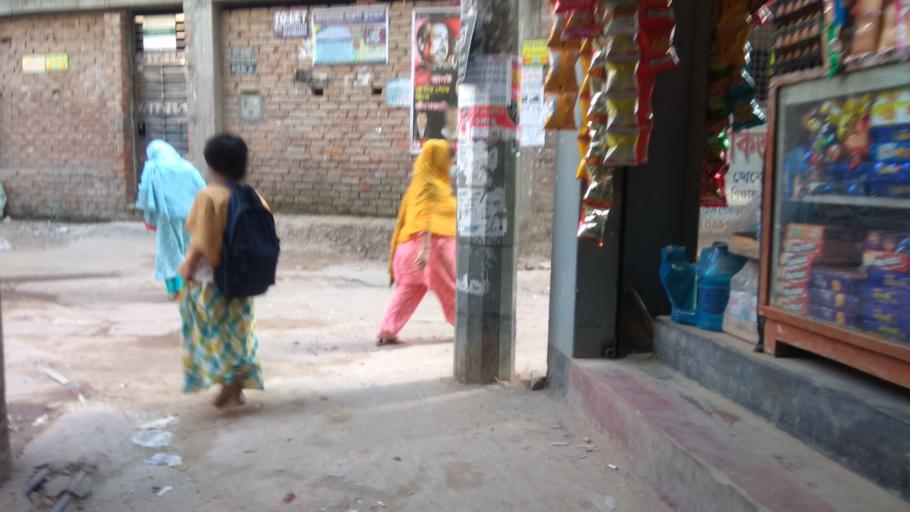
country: BD
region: Dhaka
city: Azimpur
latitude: 23.7886
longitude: 90.3733
